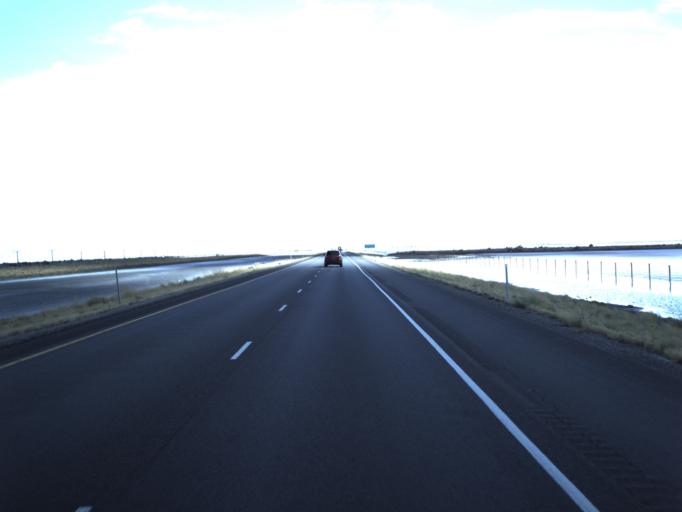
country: US
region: Utah
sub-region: Tooele County
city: Grantsville
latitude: 40.7237
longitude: -112.5680
